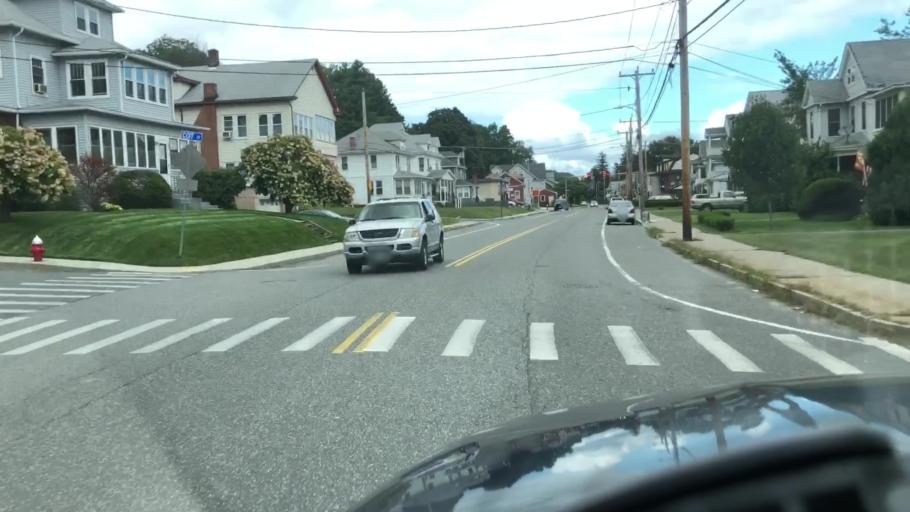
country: US
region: Massachusetts
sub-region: Hampden County
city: Holyoke
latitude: 42.1974
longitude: -72.6342
